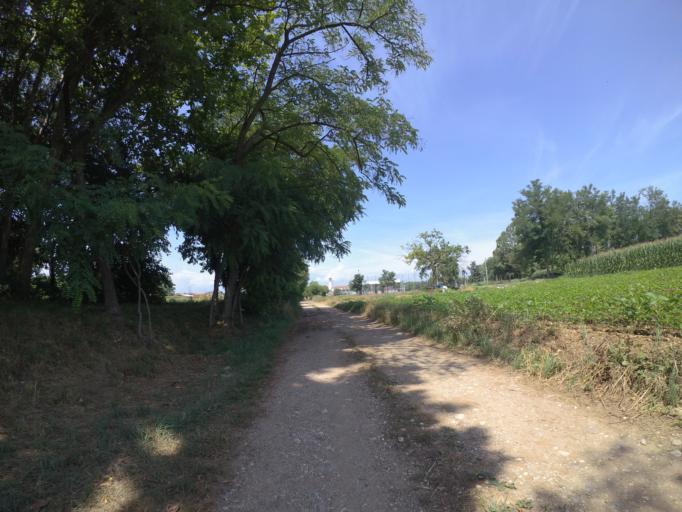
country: IT
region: Friuli Venezia Giulia
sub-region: Provincia di Udine
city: Basiliano
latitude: 45.9781
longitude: 13.0921
